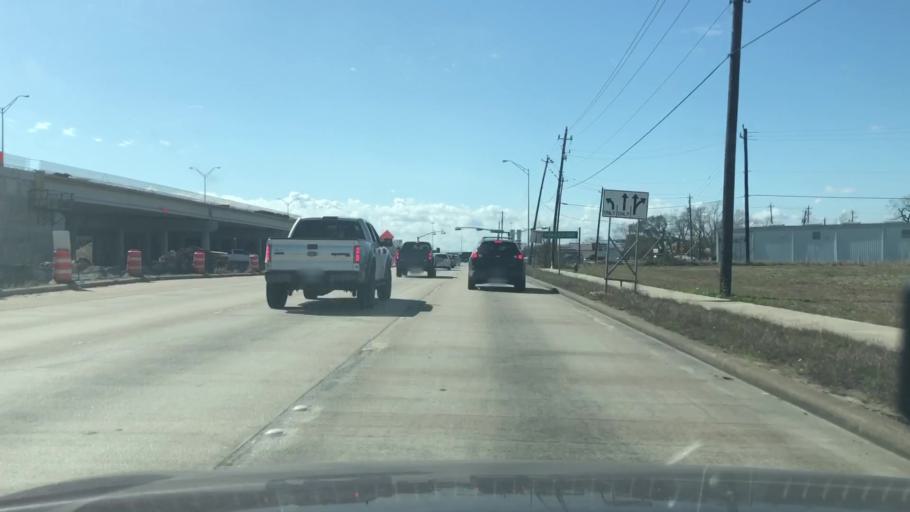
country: US
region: Texas
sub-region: Harris County
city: Pasadena
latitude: 29.6317
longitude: -95.1700
